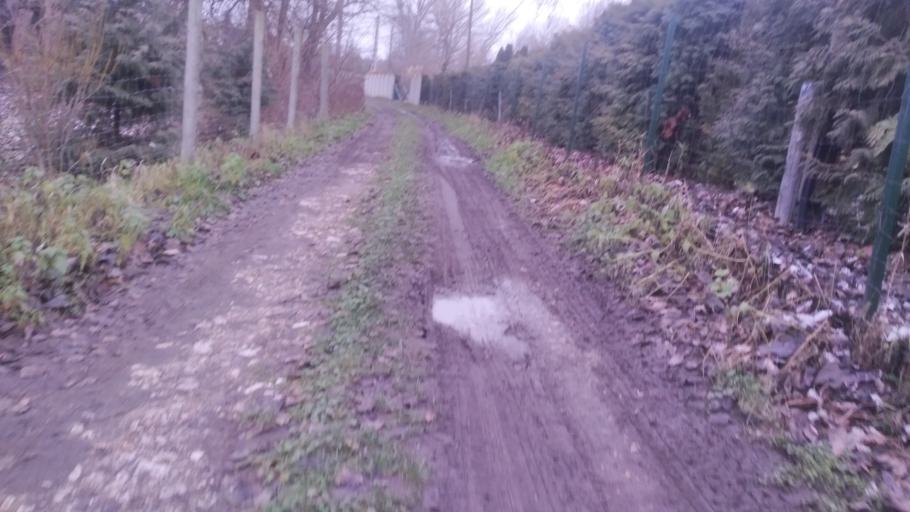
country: HU
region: Komarom-Esztergom
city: Dunaalmas
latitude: 47.7312
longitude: 18.3222
